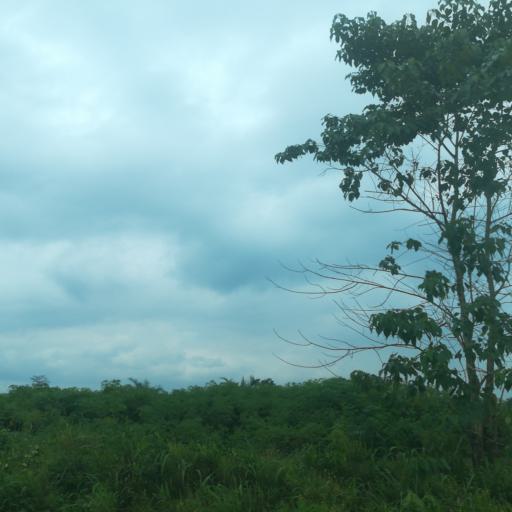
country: NG
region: Lagos
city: Ejirin
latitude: 6.6535
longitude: 3.8243
